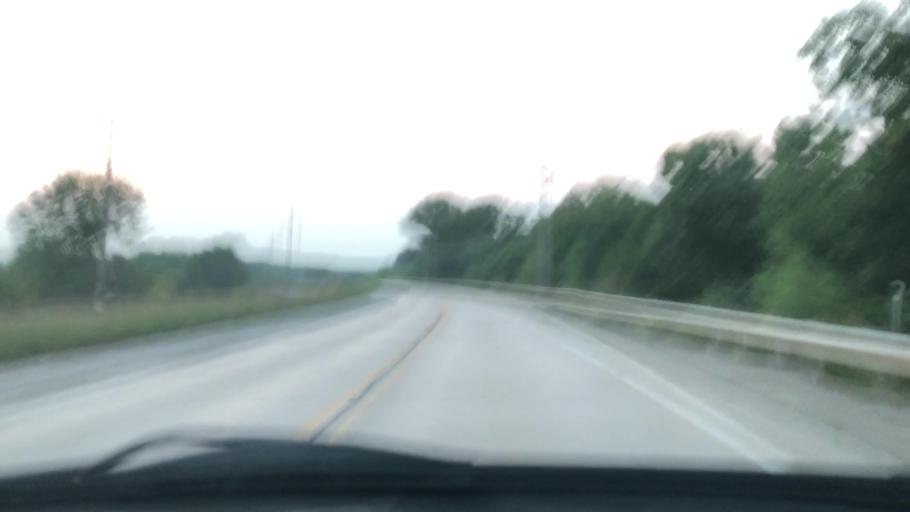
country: US
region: Iowa
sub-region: Johnson County
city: North Liberty
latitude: 41.8097
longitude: -91.6555
